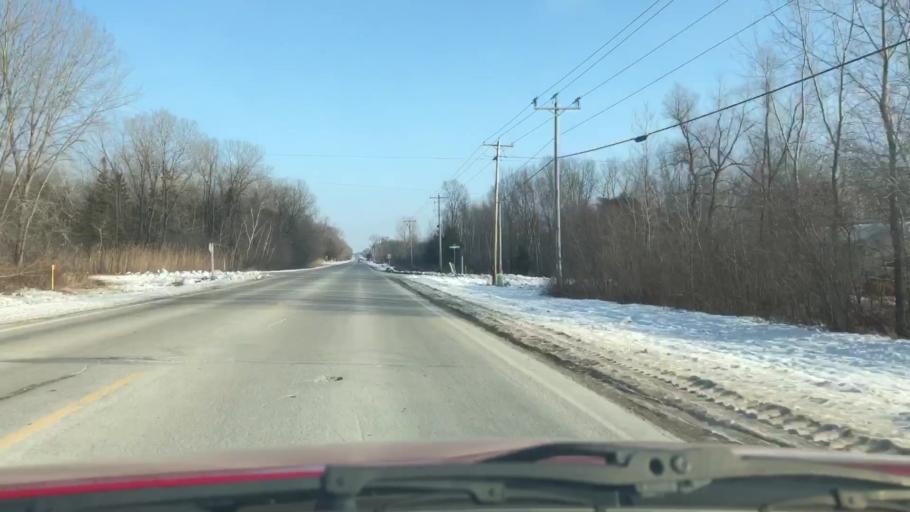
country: US
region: Wisconsin
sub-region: Outagamie County
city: Appleton
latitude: 44.3168
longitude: -88.4315
